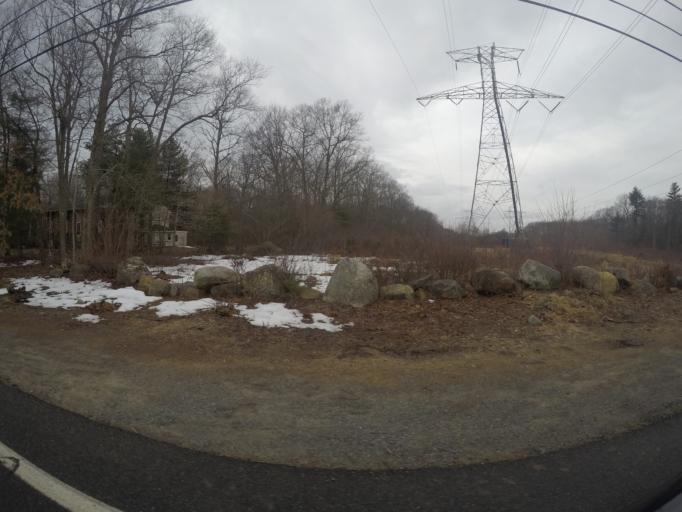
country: US
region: Massachusetts
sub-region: Bristol County
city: Easton
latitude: 42.0505
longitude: -71.1621
